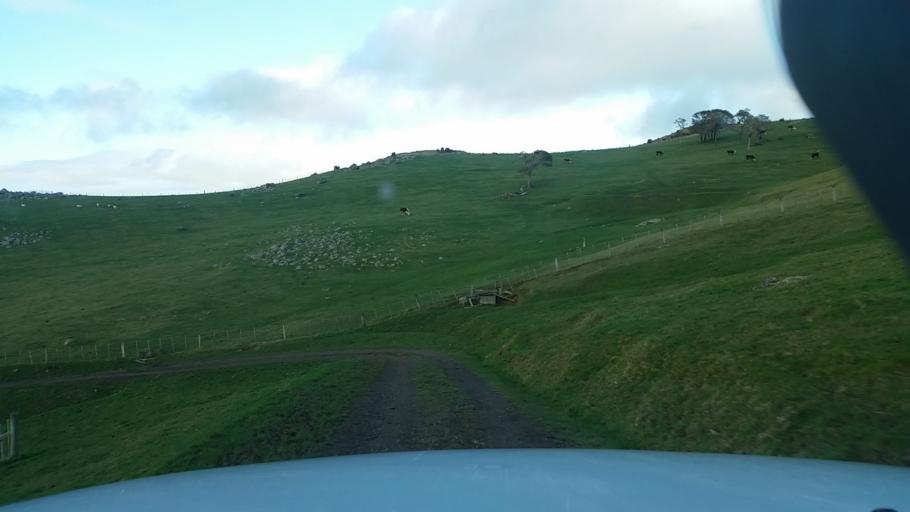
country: NZ
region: Canterbury
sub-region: Christchurch City
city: Christchurch
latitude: -43.6573
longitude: 172.8692
